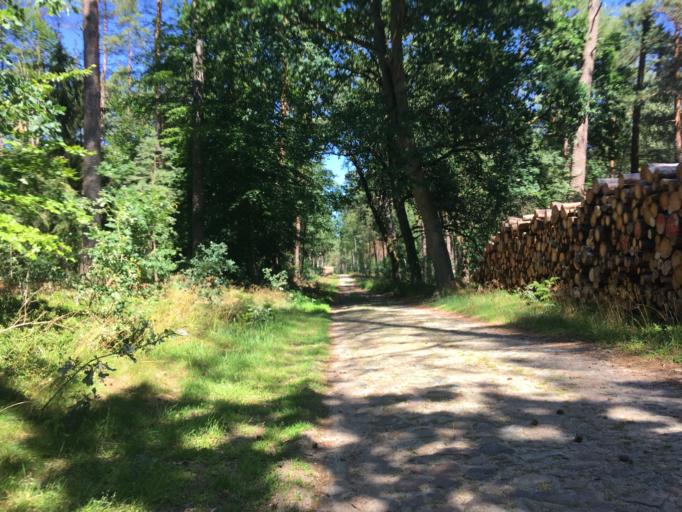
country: DE
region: Brandenburg
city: Rheinsberg
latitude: 53.1121
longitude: 12.9572
